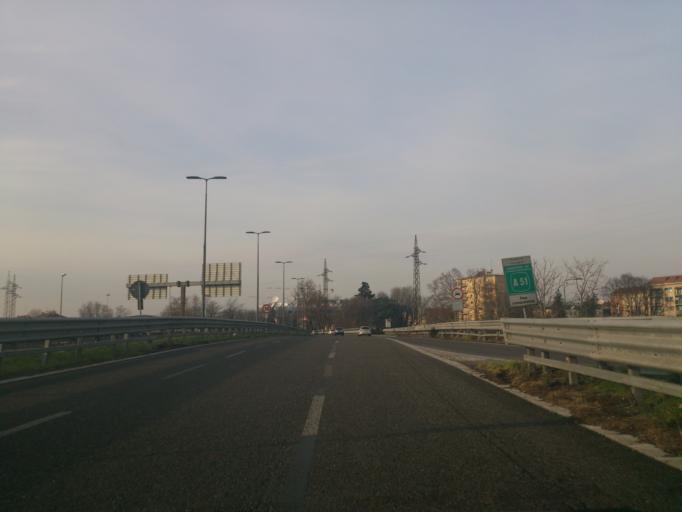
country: IT
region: Lombardy
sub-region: Citta metropolitana di Milano
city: Chiaravalle
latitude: 45.4284
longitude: 9.2447
